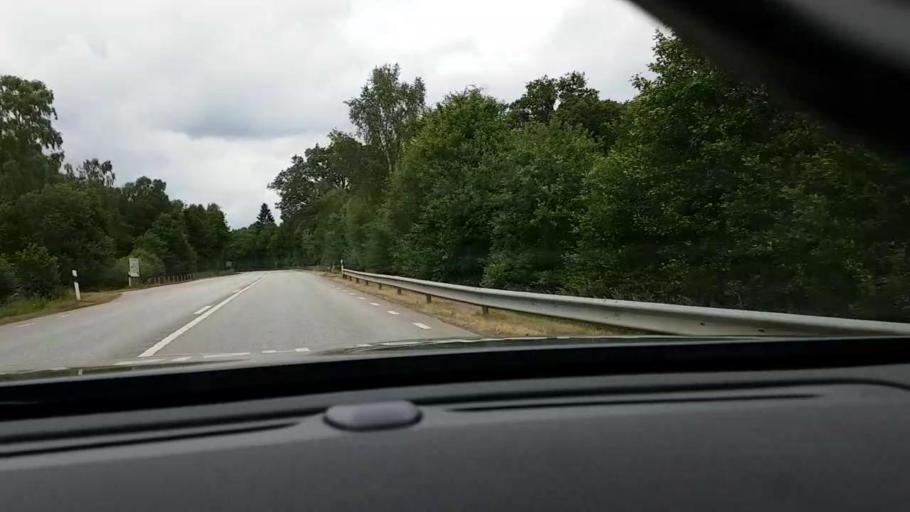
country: SE
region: Skane
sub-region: Horby Kommun
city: Hoerby
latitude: 55.8653
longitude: 13.6385
